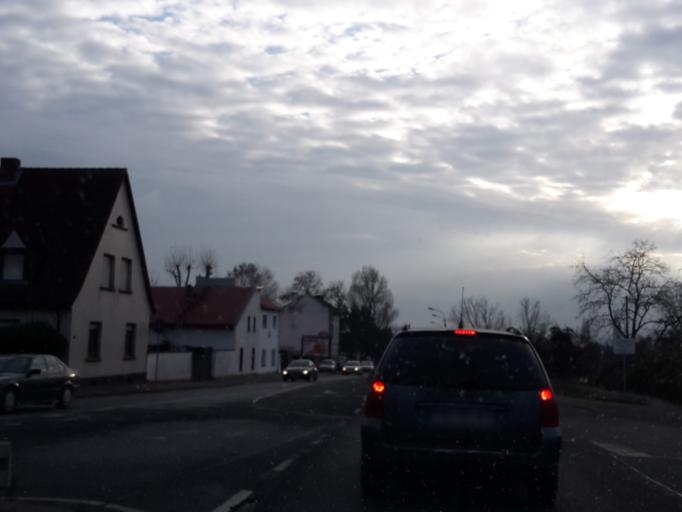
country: DE
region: Rheinland-Pfalz
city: Mainz
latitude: 50.0299
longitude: 8.2935
